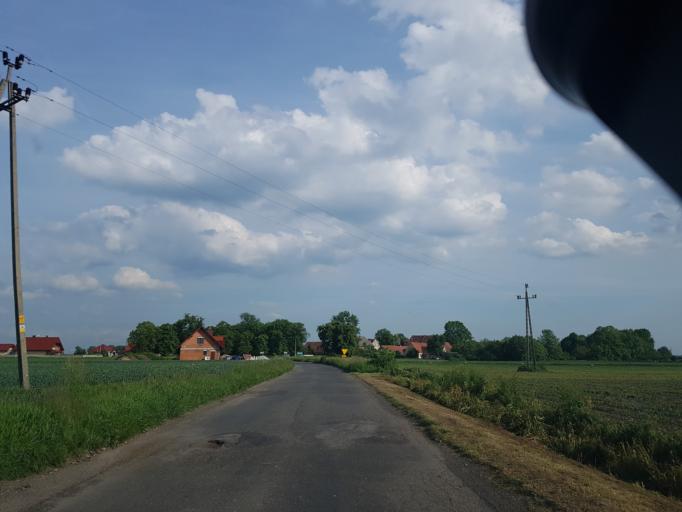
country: PL
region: Lower Silesian Voivodeship
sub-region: Powiat olawski
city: Wierzbno
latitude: 50.8711
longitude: 17.1540
